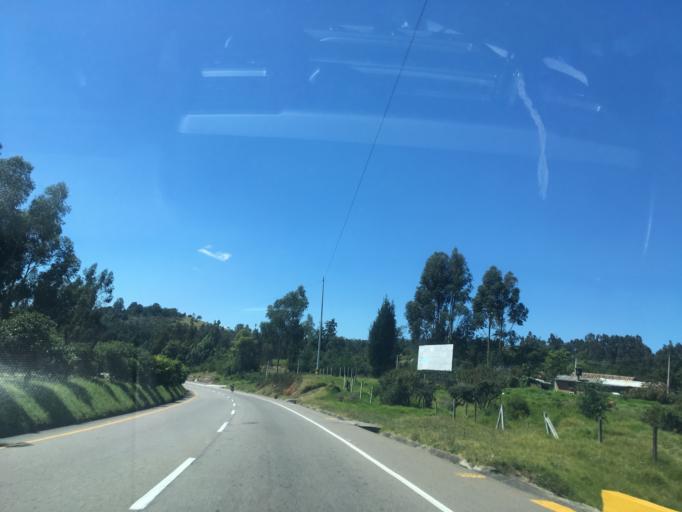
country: CO
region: Boyaca
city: Tuta
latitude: 5.6885
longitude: -73.2622
